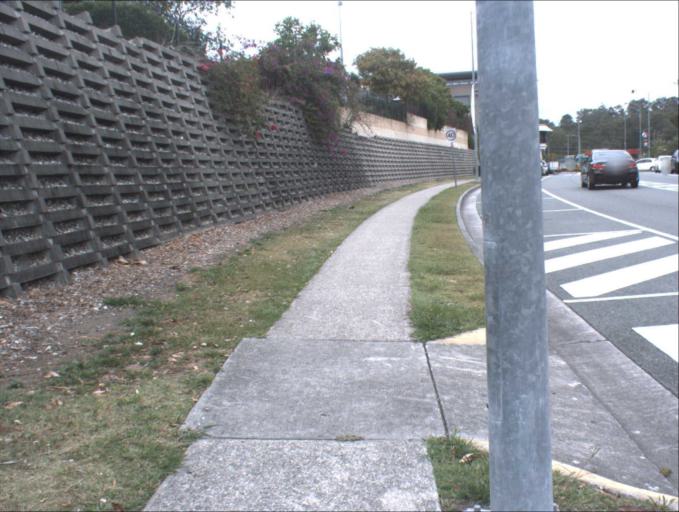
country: AU
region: Queensland
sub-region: Logan
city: Slacks Creek
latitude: -27.6573
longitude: 153.1697
